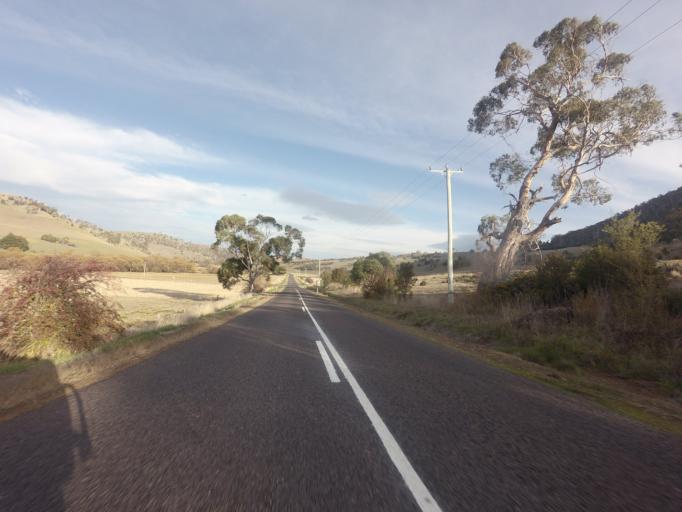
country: AU
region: Tasmania
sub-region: Brighton
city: Bridgewater
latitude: -42.4285
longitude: 147.1421
